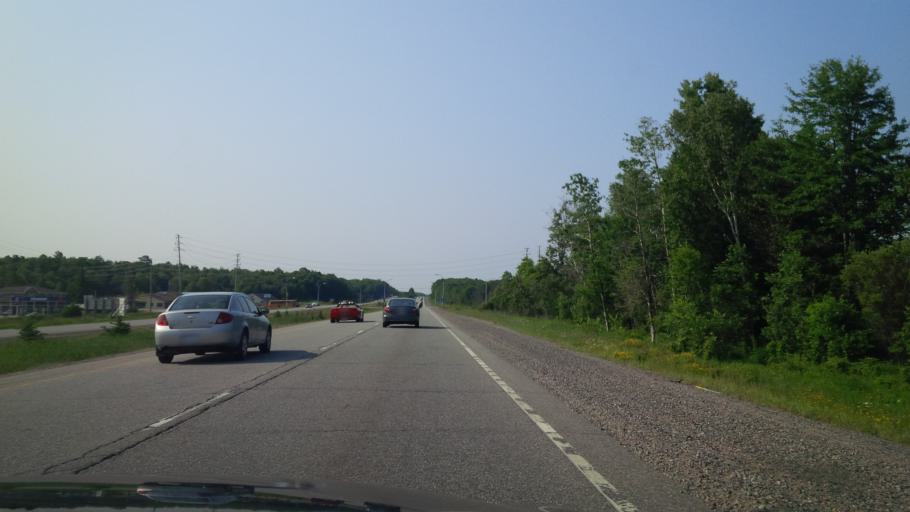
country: CA
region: Ontario
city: Bracebridge
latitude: 45.1991
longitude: -79.3143
